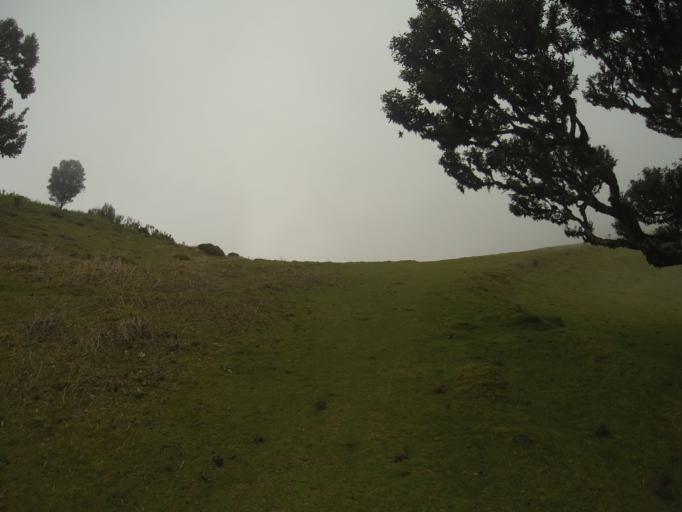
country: PT
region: Madeira
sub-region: Porto Moniz
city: Porto Moniz
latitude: 32.8137
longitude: -17.1444
